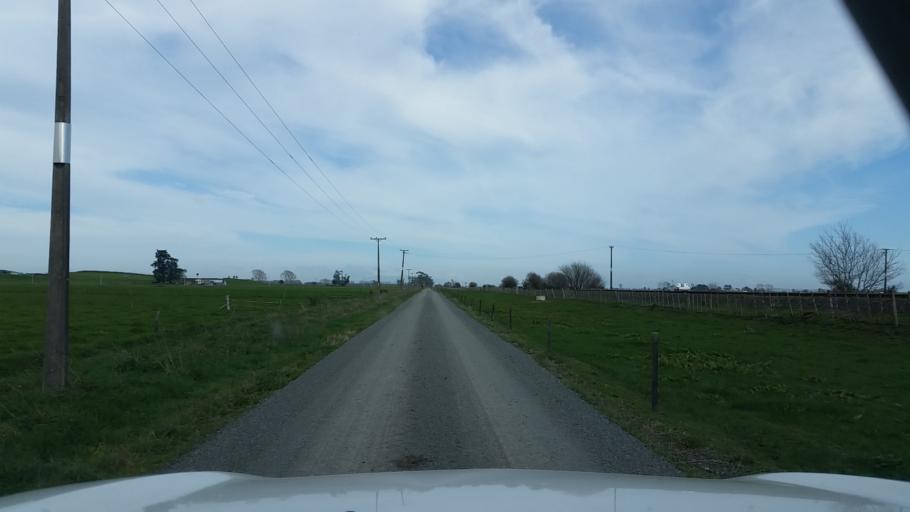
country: NZ
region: Waikato
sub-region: Waipa District
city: Cambridge
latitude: -37.6776
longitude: 175.4613
